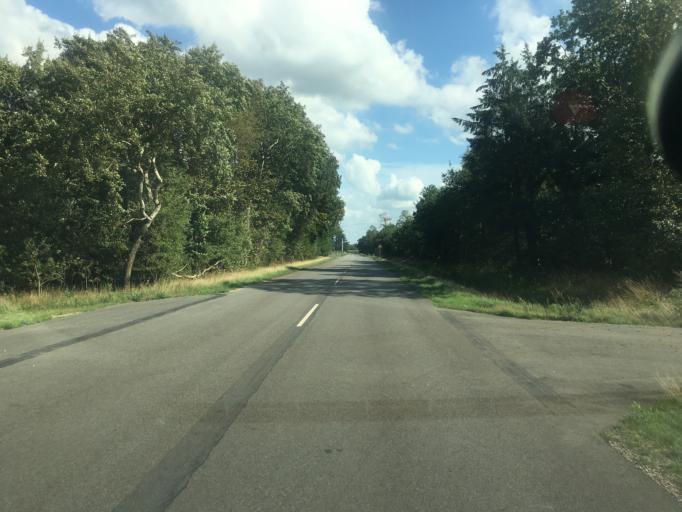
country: DE
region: Schleswig-Holstein
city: Ellhoft
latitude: 54.9675
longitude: 8.9719
